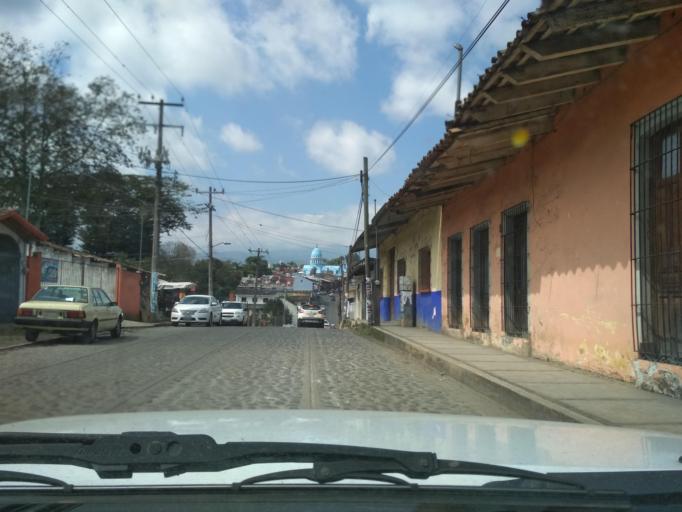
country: MX
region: Veracruz
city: Coatepec
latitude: 19.4515
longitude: -96.9503
